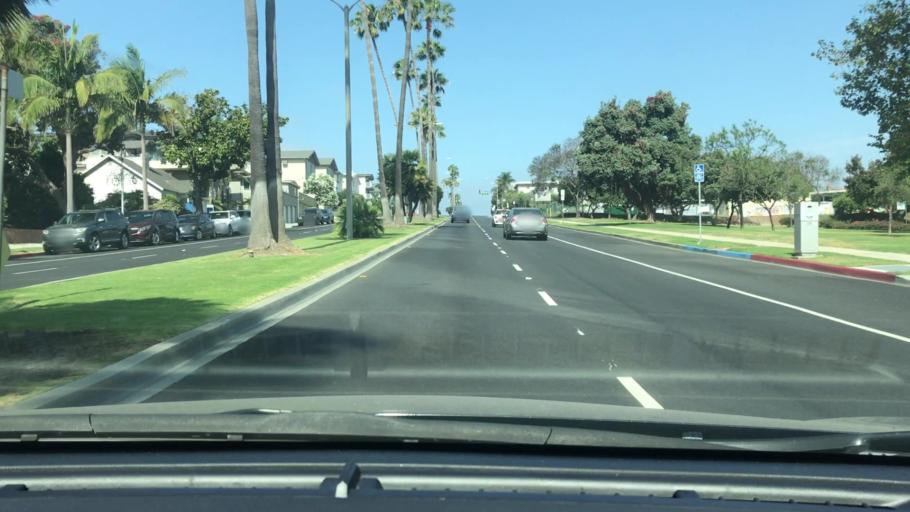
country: US
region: California
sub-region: Los Angeles County
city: Manhattan Beach
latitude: 33.8874
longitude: -118.3851
